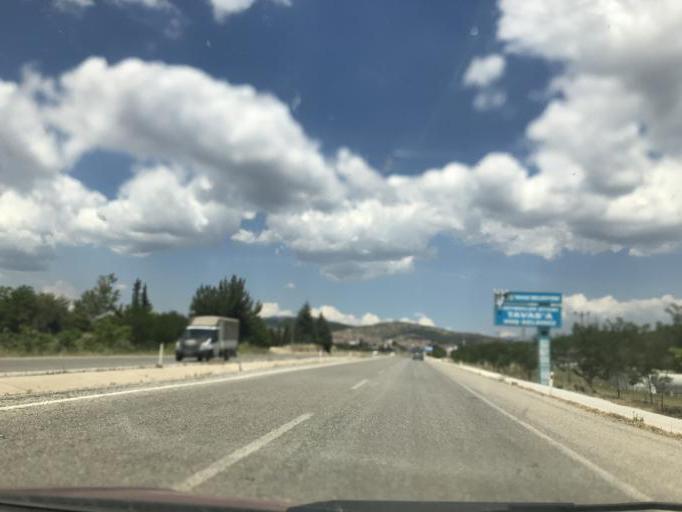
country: TR
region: Denizli
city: Tavas
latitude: 37.5562
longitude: 29.0559
